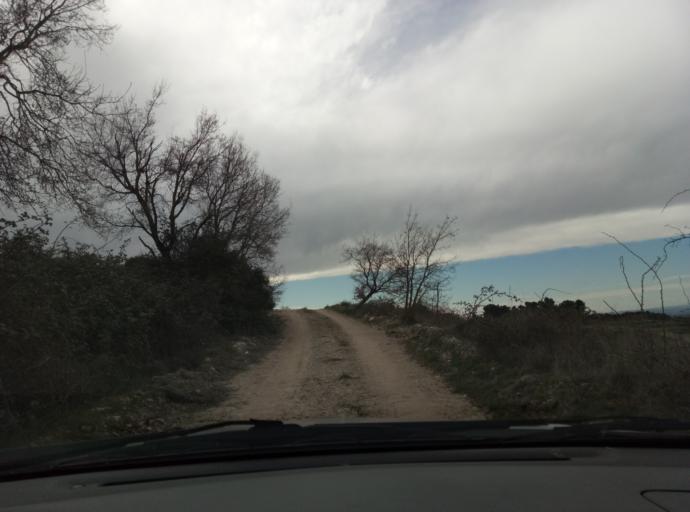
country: ES
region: Catalonia
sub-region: Provincia de Lleida
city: Ciutadilla
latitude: 41.5191
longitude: 1.1638
